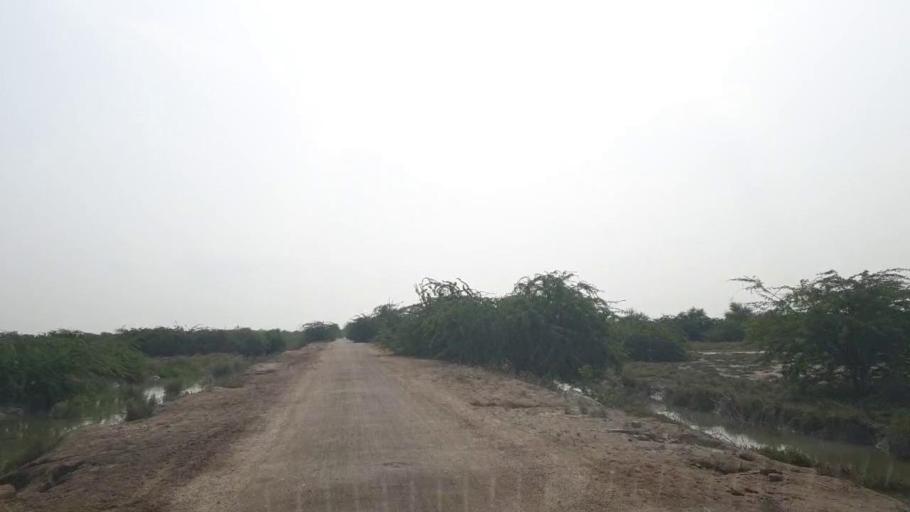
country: PK
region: Sindh
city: Badin
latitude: 24.5514
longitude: 68.6877
